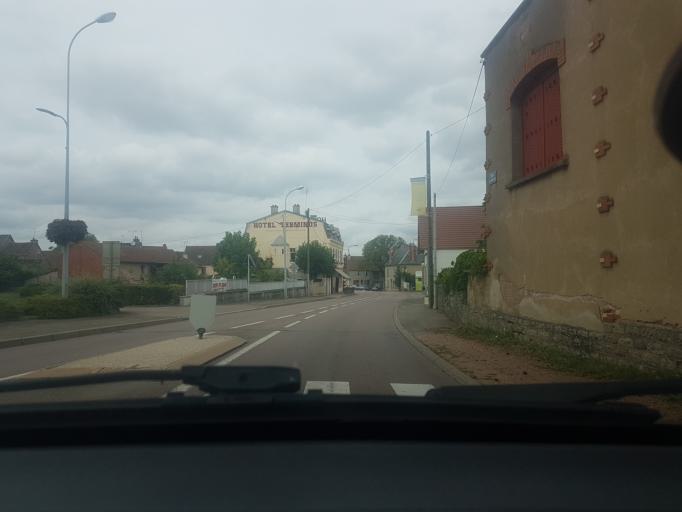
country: FR
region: Bourgogne
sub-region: Departement de la Cote-d'Or
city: Arnay-le-Duc
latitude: 47.1306
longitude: 4.4898
